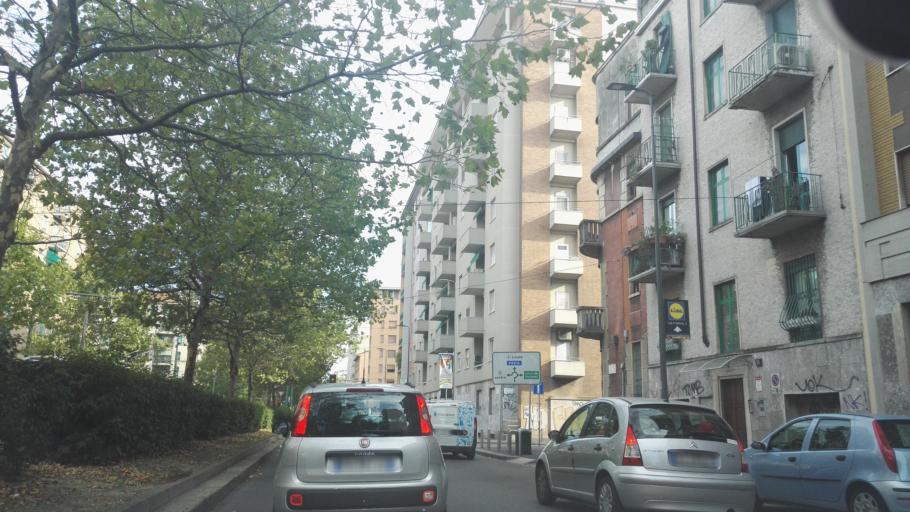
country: IT
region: Lombardy
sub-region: Citta metropolitana di Milano
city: Milano
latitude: 45.4563
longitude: 9.1519
